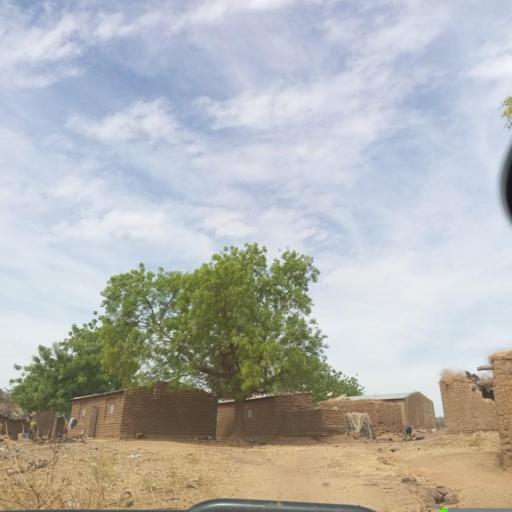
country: ML
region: Koulikoro
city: Koulikoro
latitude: 13.1687
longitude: -7.7300
